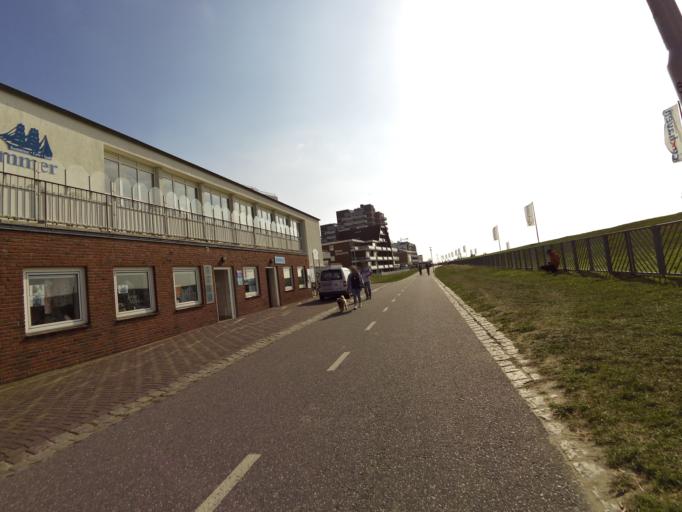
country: DE
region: Lower Saxony
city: Cuxhaven
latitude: 53.8865
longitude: 8.6440
